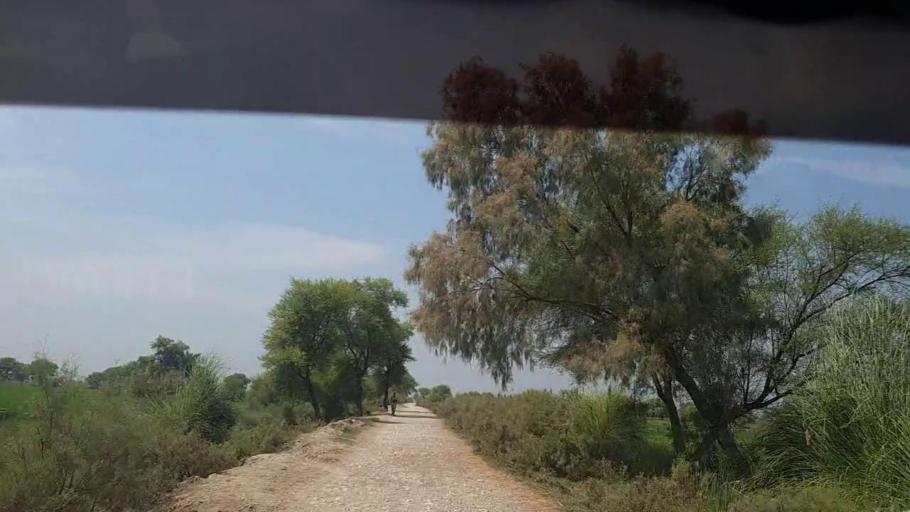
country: PK
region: Sindh
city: Thul
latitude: 28.2068
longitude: 68.6925
